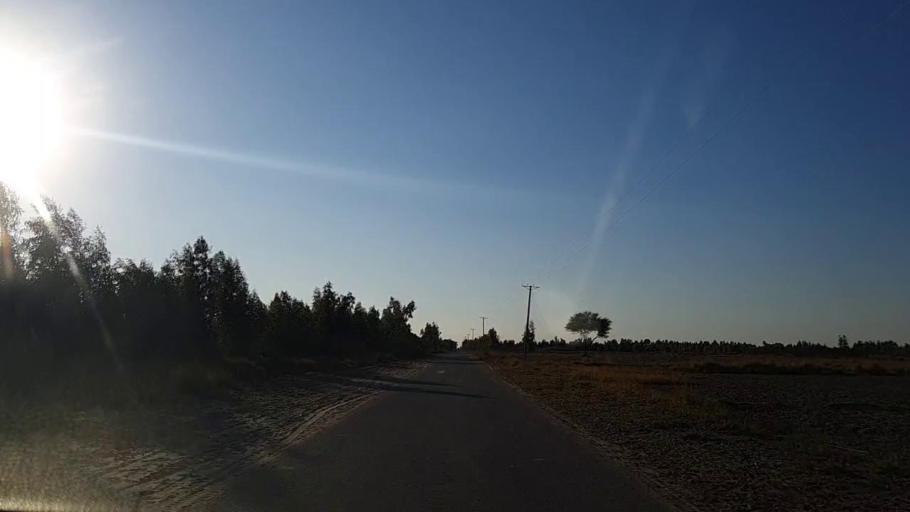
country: PK
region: Sindh
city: Khadro
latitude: 26.2790
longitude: 68.9047
